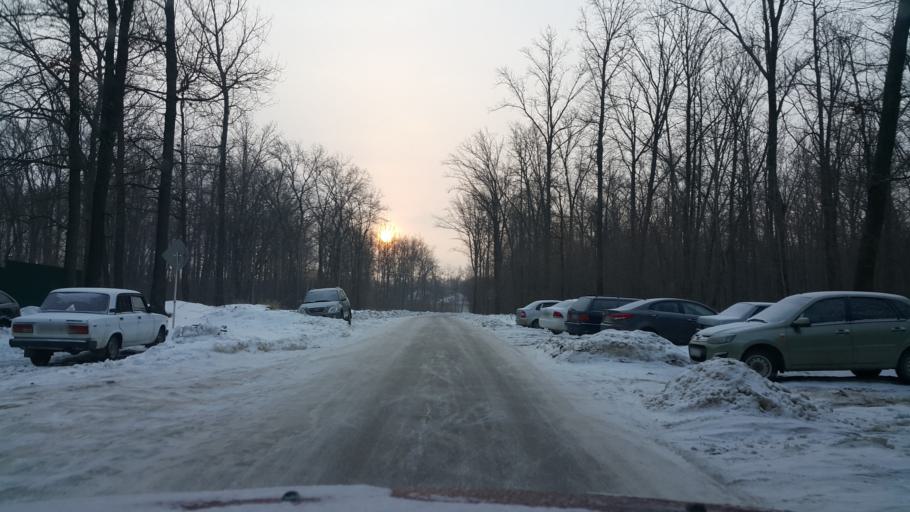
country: RU
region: Tambov
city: Kotovsk
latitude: 52.5741
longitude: 41.5185
